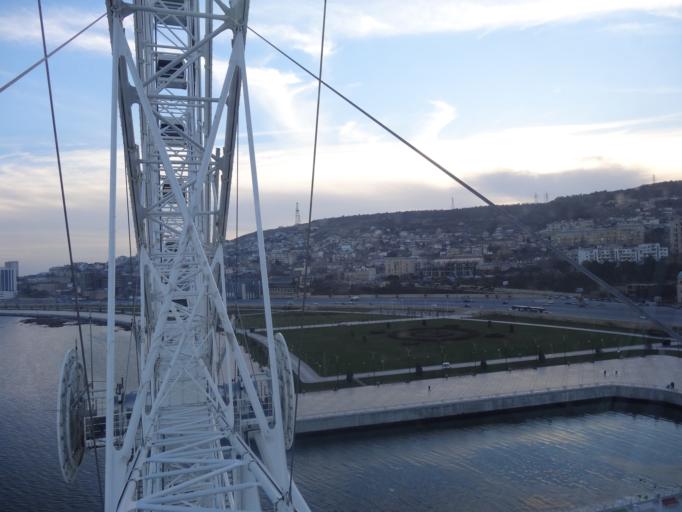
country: AZ
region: Baki
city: Badamdar
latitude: 40.3549
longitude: 49.8377
